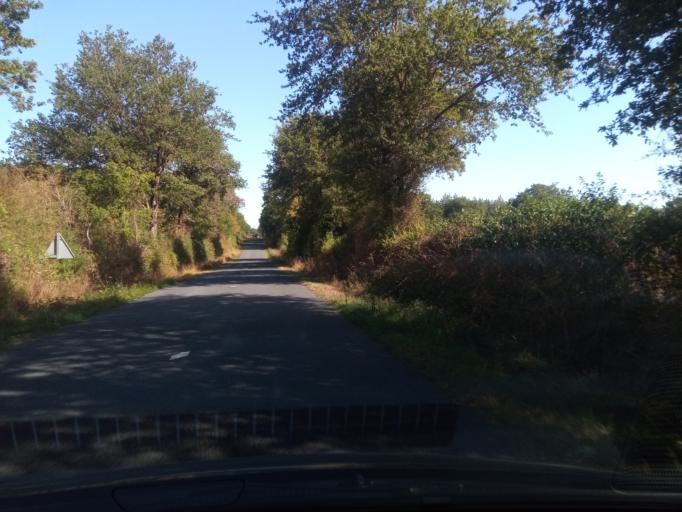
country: FR
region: Poitou-Charentes
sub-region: Departement de la Vienne
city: Saulge
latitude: 46.3460
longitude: 0.8696
